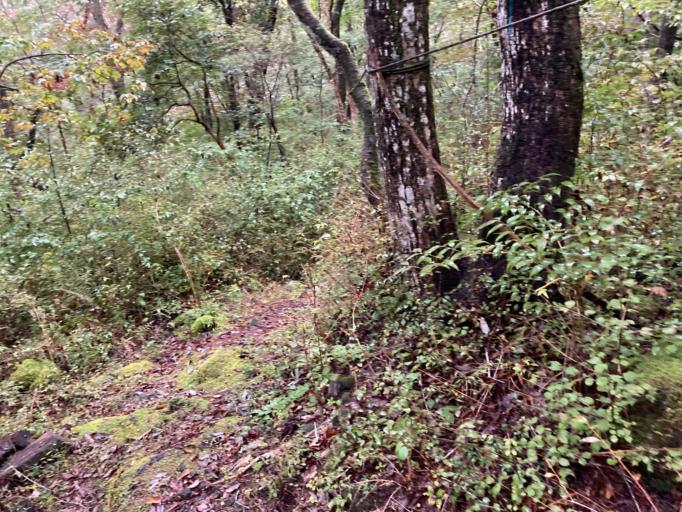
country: JP
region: Shizuoka
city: Fuji
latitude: 35.2439
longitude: 138.7311
